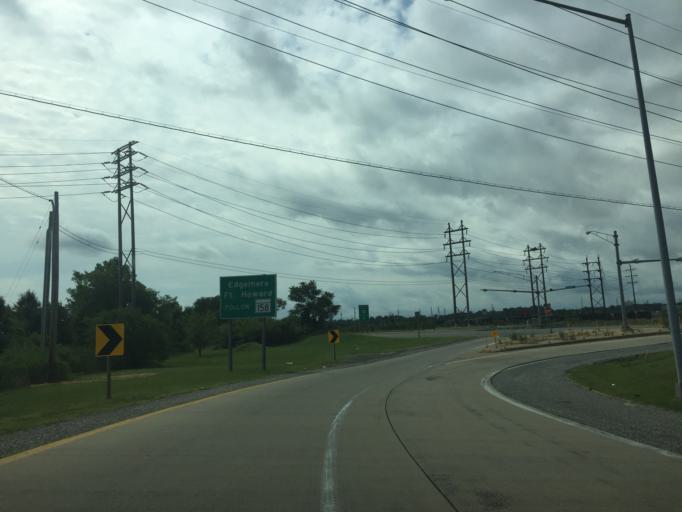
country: US
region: Maryland
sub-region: Baltimore County
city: Edgemere
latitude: 39.2375
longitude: -76.4760
